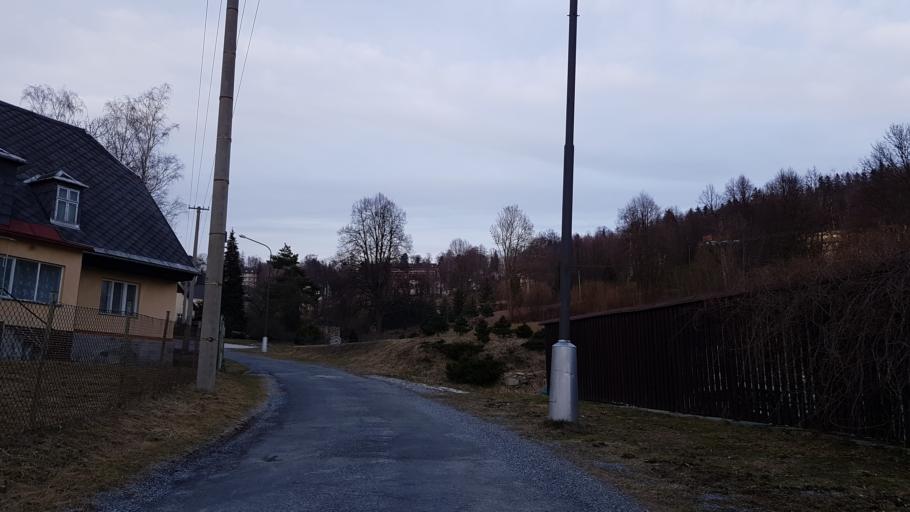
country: CZ
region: Olomoucky
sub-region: Okres Jesenik
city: Jesenik
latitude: 50.2352
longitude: 17.1861
